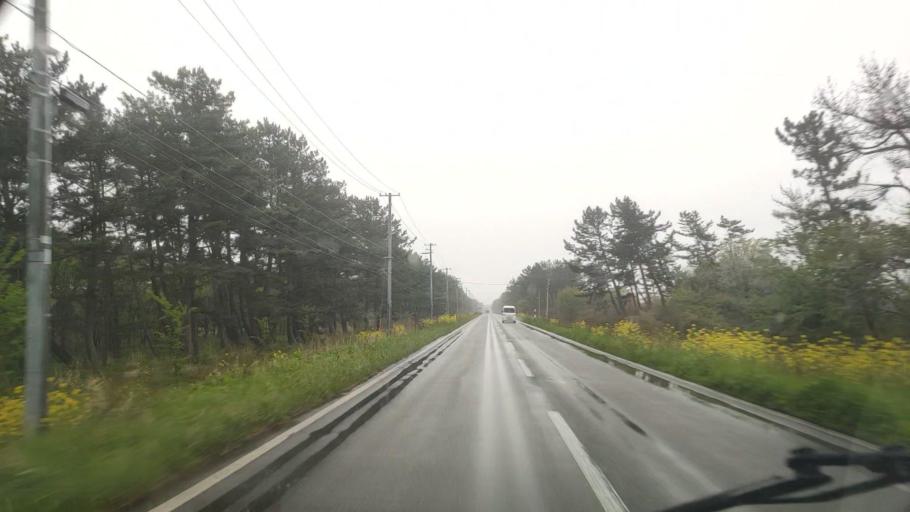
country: JP
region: Akita
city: Tenno
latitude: 40.0277
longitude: 139.9526
